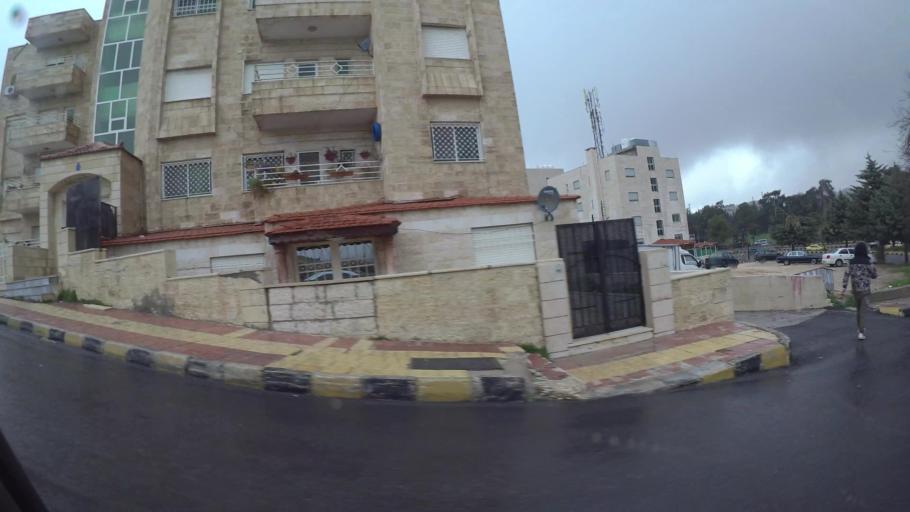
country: JO
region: Amman
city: Al Jubayhah
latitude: 32.0163
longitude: 35.8424
